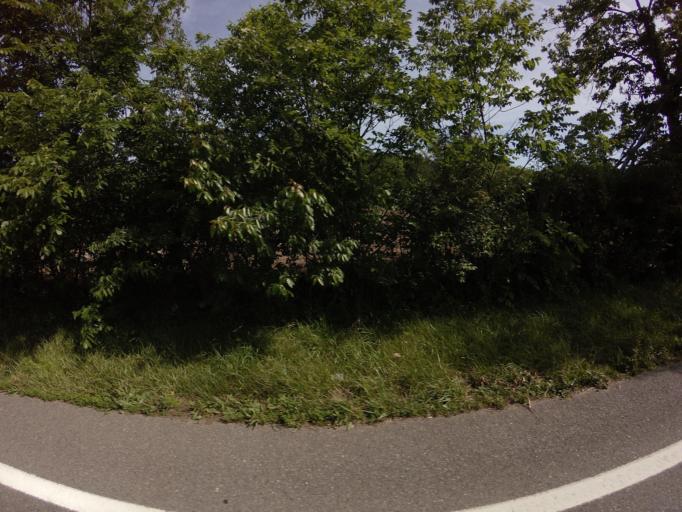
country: US
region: Maryland
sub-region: Frederick County
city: Green Valley
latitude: 39.3476
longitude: -77.2945
